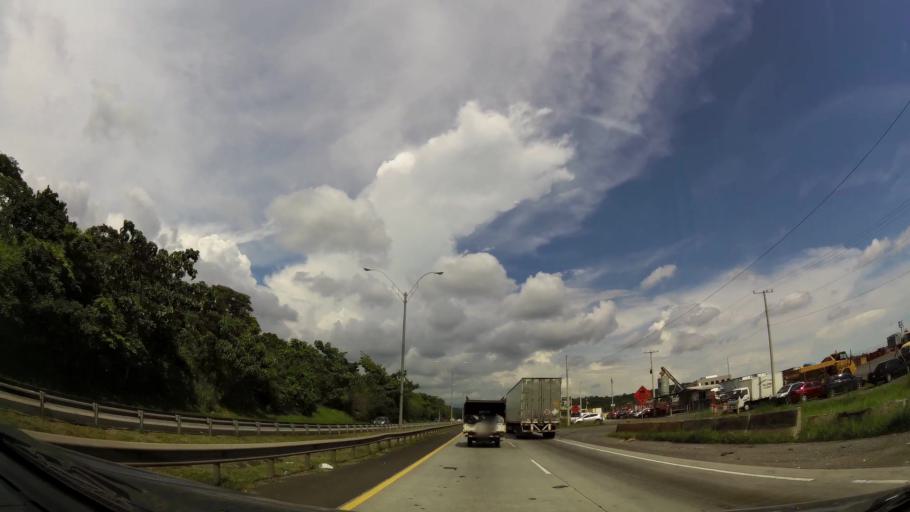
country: PA
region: Panama
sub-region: Distrito de Panama
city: Paraiso
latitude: 9.0310
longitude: -79.5840
